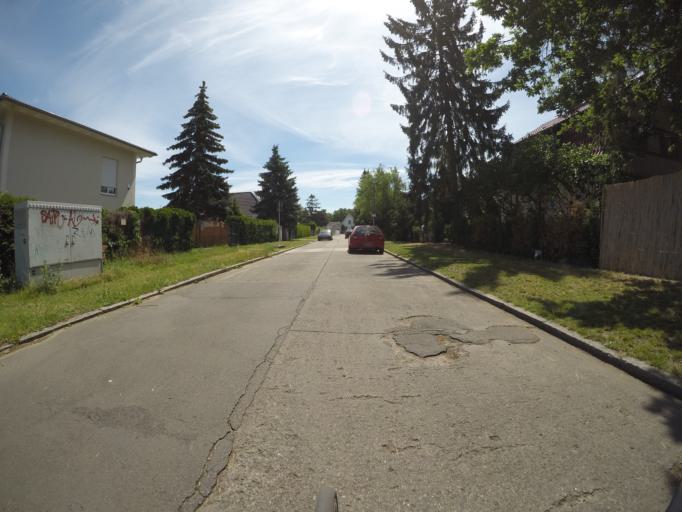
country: DE
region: Berlin
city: Kaulsdorf
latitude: 52.4964
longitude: 13.5827
